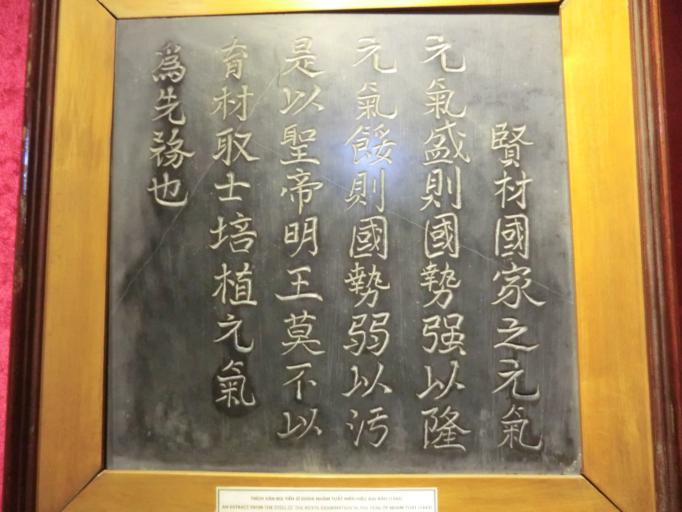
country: VN
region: Ha Noi
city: Hanoi
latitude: 21.0304
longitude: 105.8364
